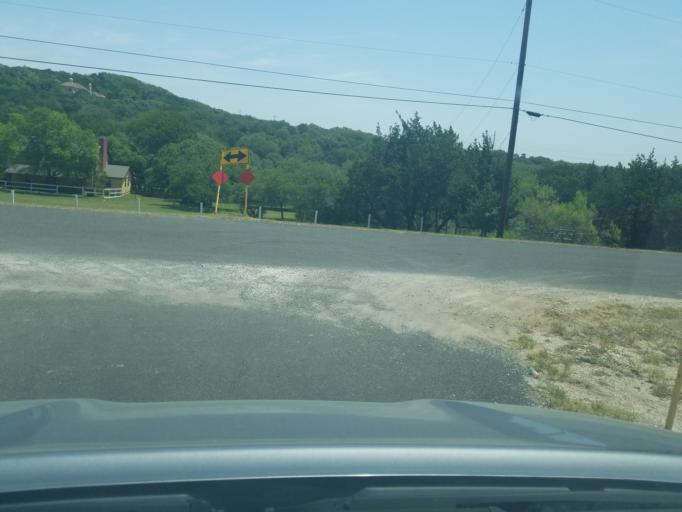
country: US
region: Texas
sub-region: Bexar County
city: Timberwood Park
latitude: 29.6722
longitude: -98.5073
